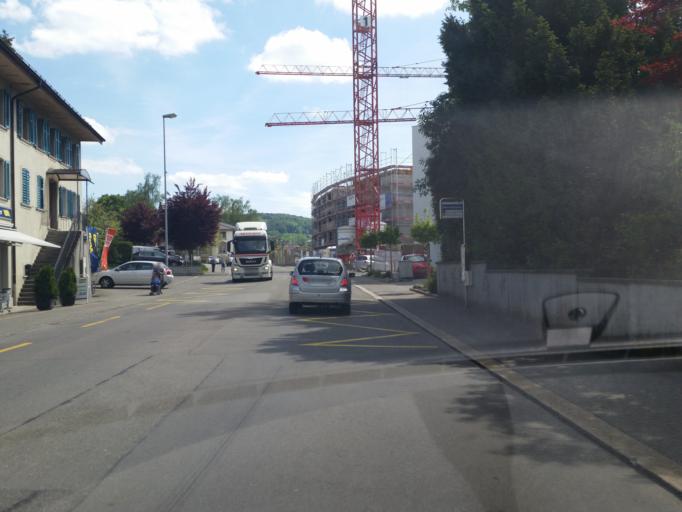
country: CH
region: Aargau
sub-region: Bezirk Bremgarten
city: Wohlen
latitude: 47.3473
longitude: 8.2769
